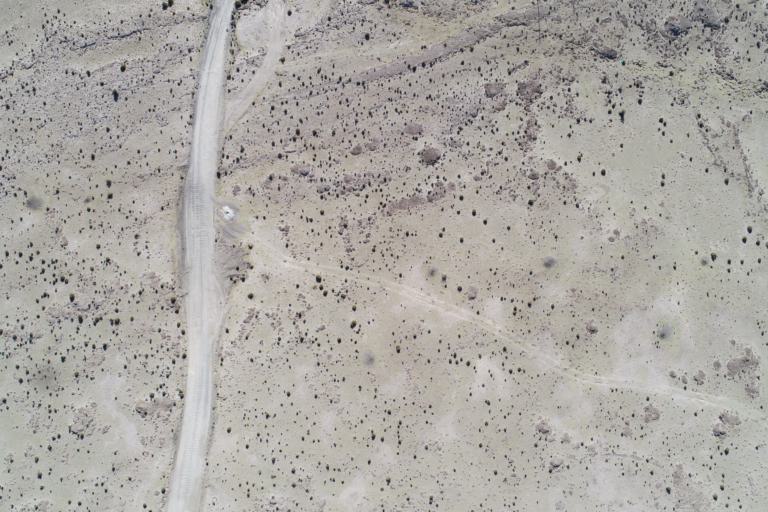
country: BO
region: Potosi
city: Colchani
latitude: -20.3521
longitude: -66.8968
